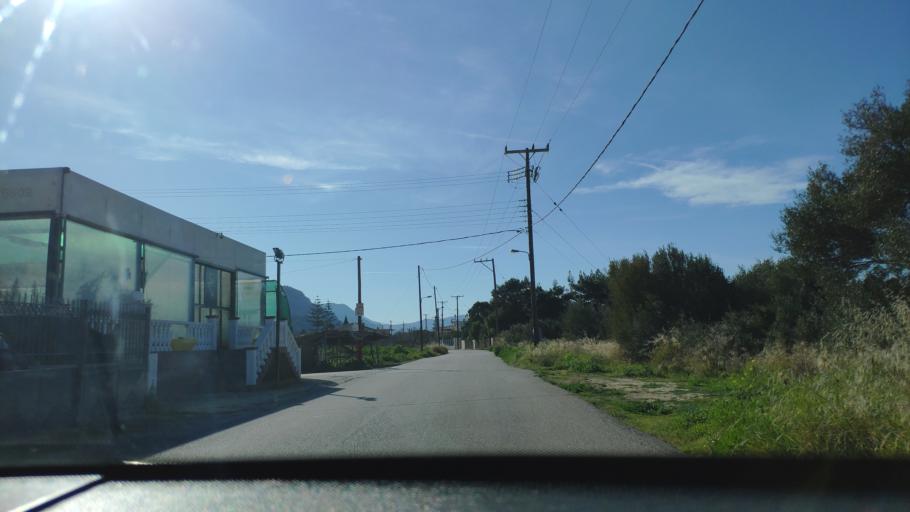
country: GR
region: Attica
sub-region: Nomarchia Dytikis Attikis
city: Kineta
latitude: 38.0709
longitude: 23.1564
